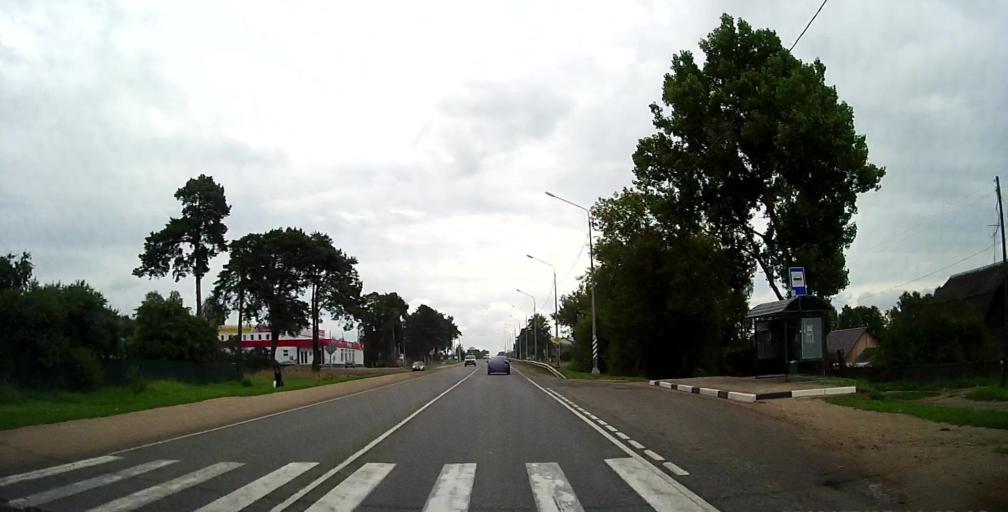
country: RU
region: Smolensk
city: Katyn'
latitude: 54.7840
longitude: 31.8404
